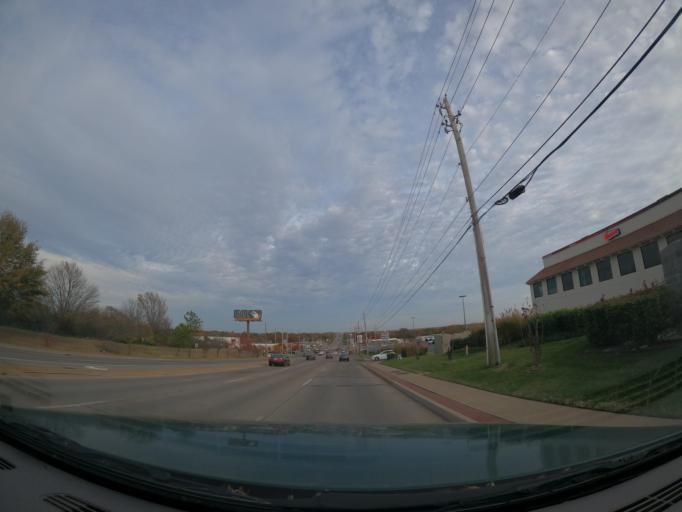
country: US
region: Oklahoma
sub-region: Tulsa County
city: Jenks
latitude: 36.0607
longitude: -95.9063
